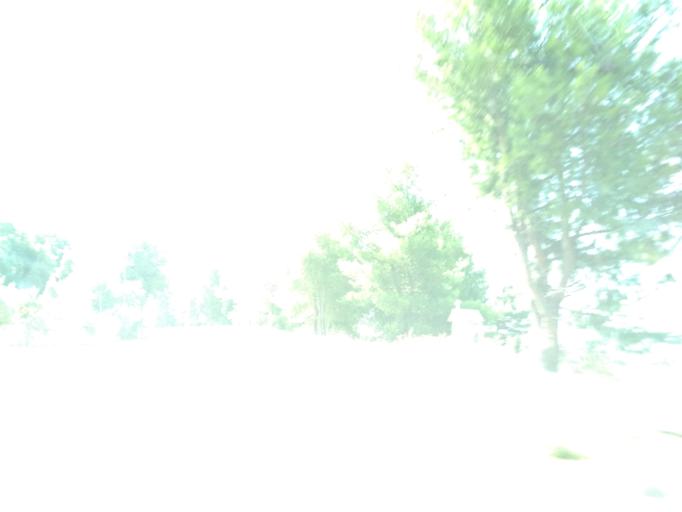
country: GR
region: Central Greece
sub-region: Nomos Evvoias
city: Roviai
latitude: 38.8262
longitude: 23.2253
